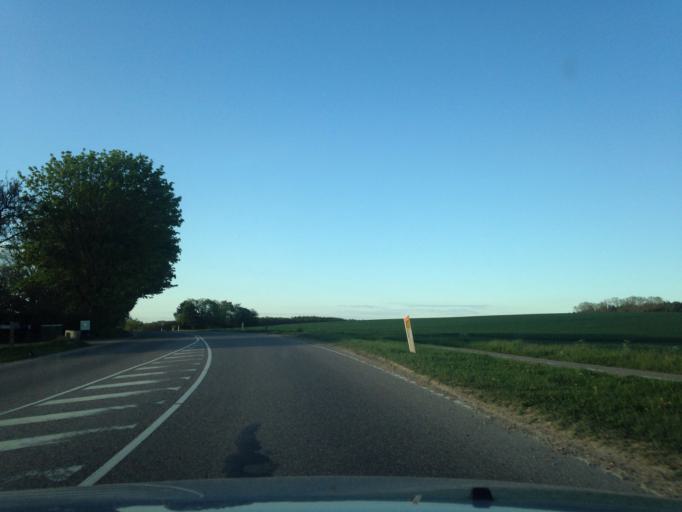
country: DK
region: Capital Region
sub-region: Hoje-Taastrup Kommune
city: Flong
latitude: 55.6313
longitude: 12.1920
